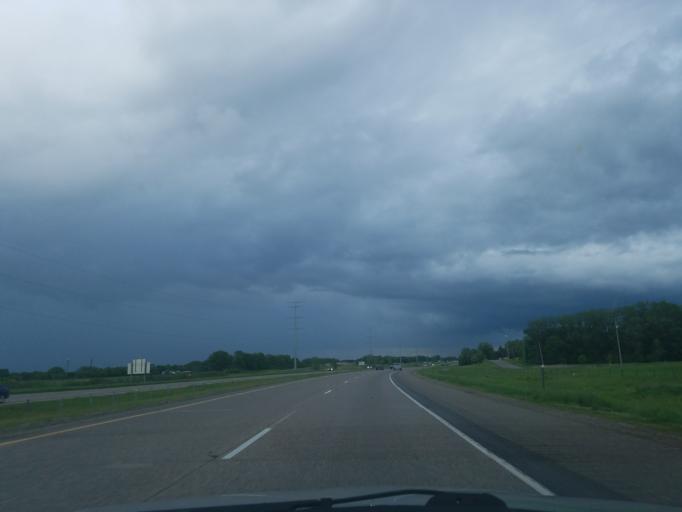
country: US
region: Minnesota
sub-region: Sherburne County
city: Becker
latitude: 45.3672
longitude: -93.9660
